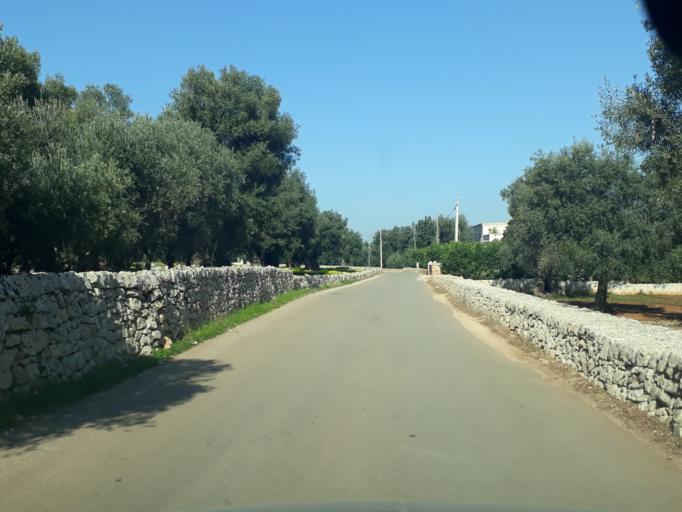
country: IT
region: Apulia
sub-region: Provincia di Brindisi
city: Fasano
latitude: 40.8417
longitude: 17.3451
